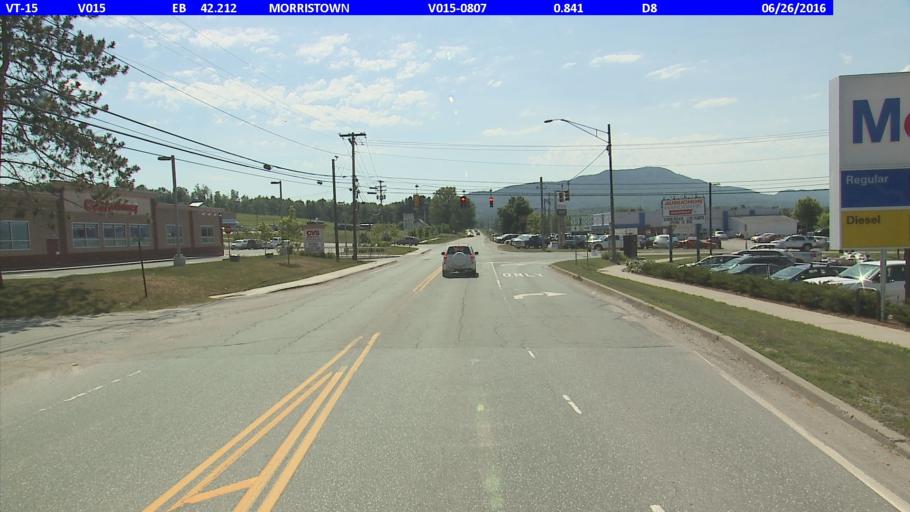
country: US
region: Vermont
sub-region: Lamoille County
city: Morrisville
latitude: 44.5760
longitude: -72.5931
